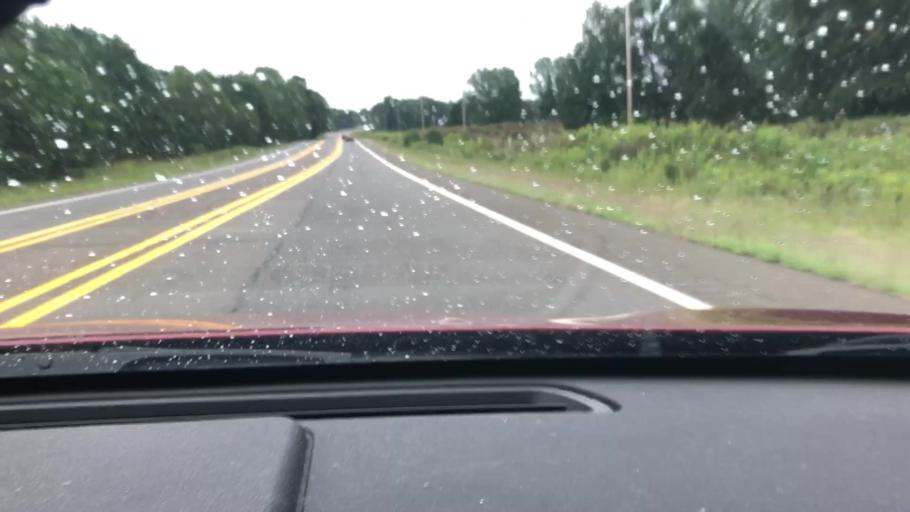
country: US
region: Arkansas
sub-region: Columbia County
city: Waldo
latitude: 33.3509
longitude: -93.3660
